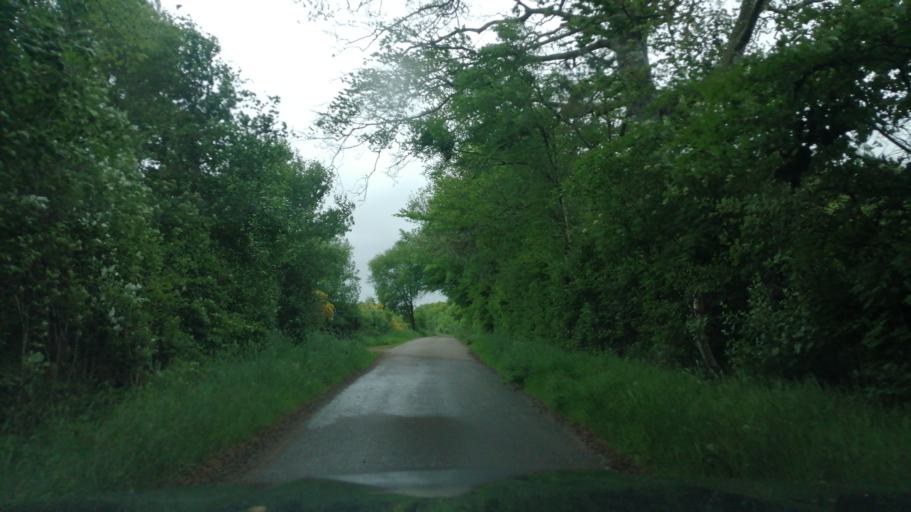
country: GB
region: Scotland
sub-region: Moray
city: Keith
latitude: 57.5620
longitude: -2.8619
